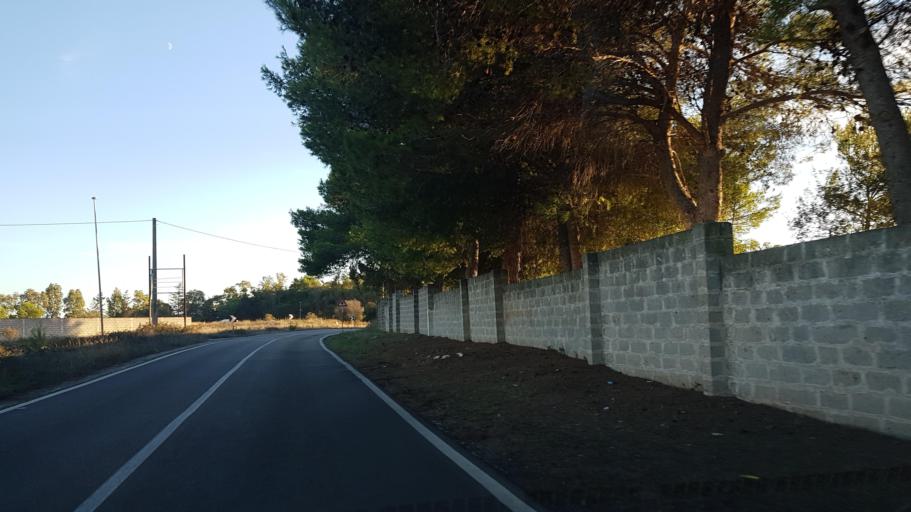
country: IT
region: Apulia
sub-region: Provincia di Lecce
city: Giorgilorio
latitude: 40.4094
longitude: 18.2010
